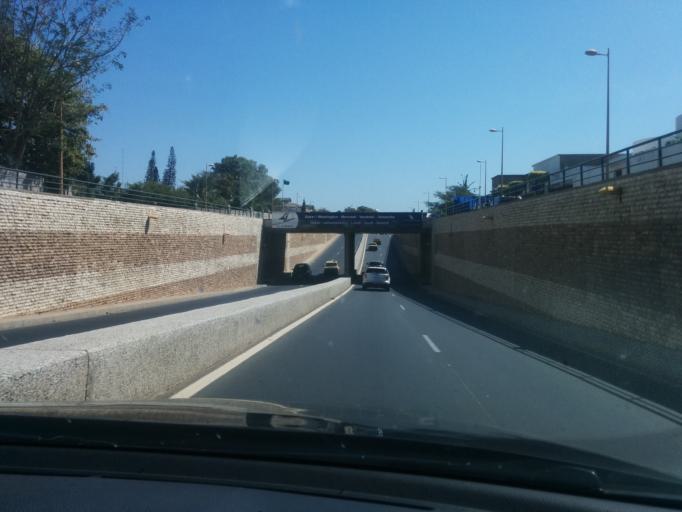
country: SN
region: Dakar
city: Mermoz Boabab
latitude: 14.7013
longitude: -17.4760
